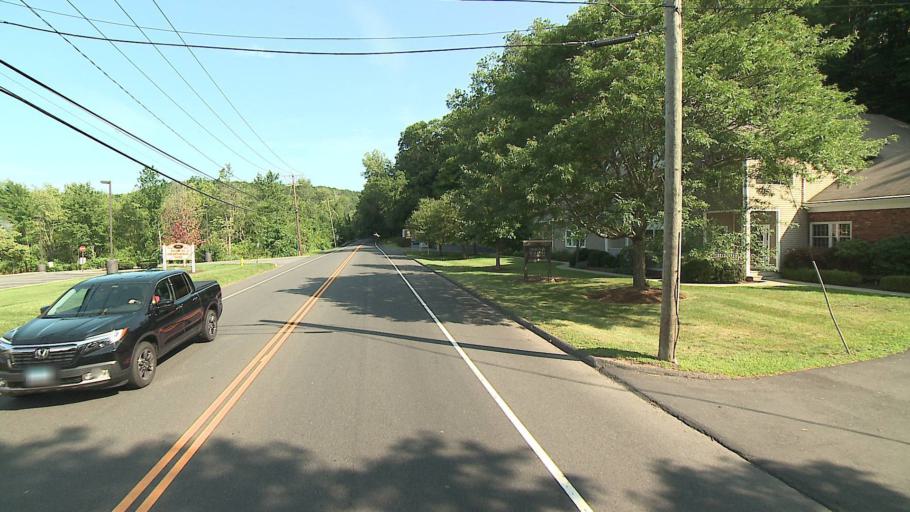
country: US
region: Connecticut
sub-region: Fairfield County
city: Ridgefield
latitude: 41.3164
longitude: -73.4737
